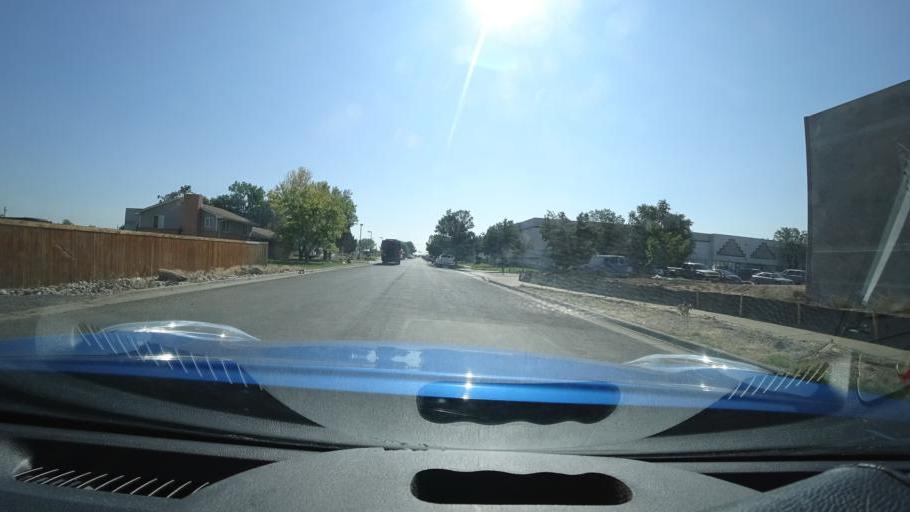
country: US
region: Colorado
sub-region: Adams County
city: Aurora
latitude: 39.7194
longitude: -104.7957
